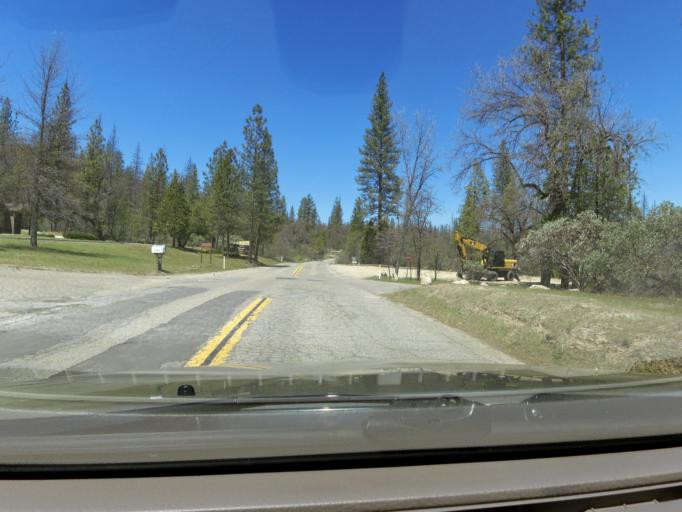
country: US
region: California
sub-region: Madera County
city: Oakhurst
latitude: 37.3277
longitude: -119.5821
